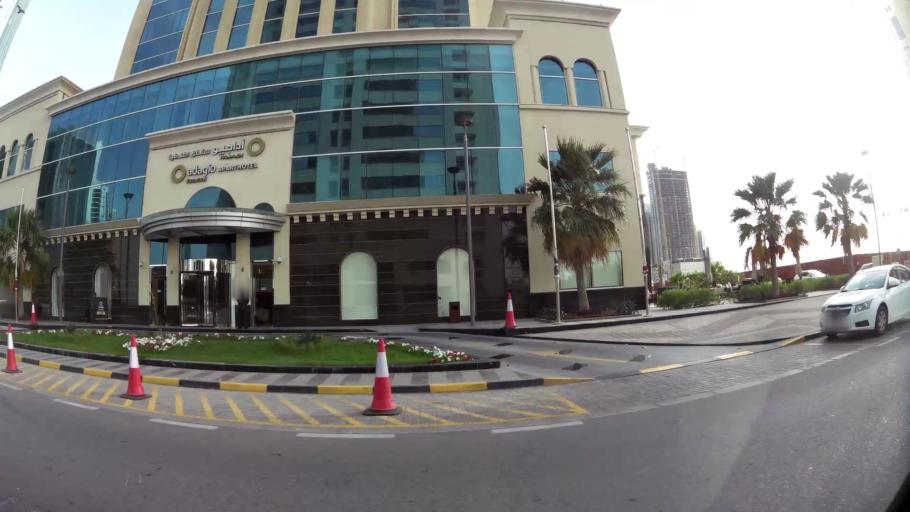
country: QA
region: Baladiyat ad Dawhah
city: Doha
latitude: 25.3249
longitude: 51.5243
